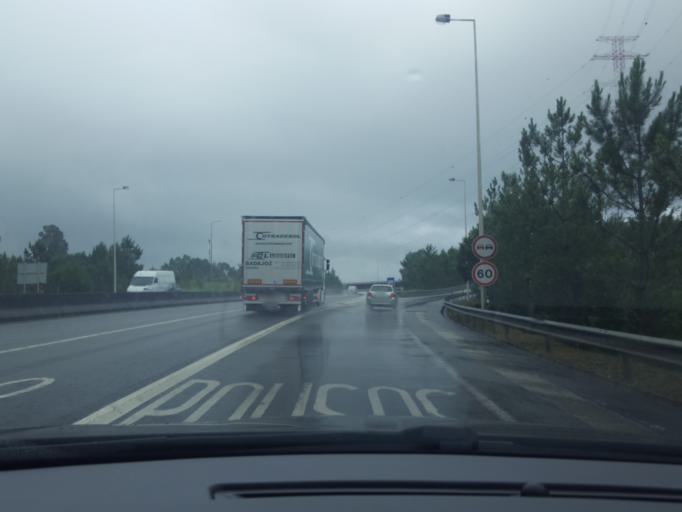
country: PT
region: Leiria
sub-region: Leiria
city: Leiria
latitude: 39.7393
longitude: -8.7689
